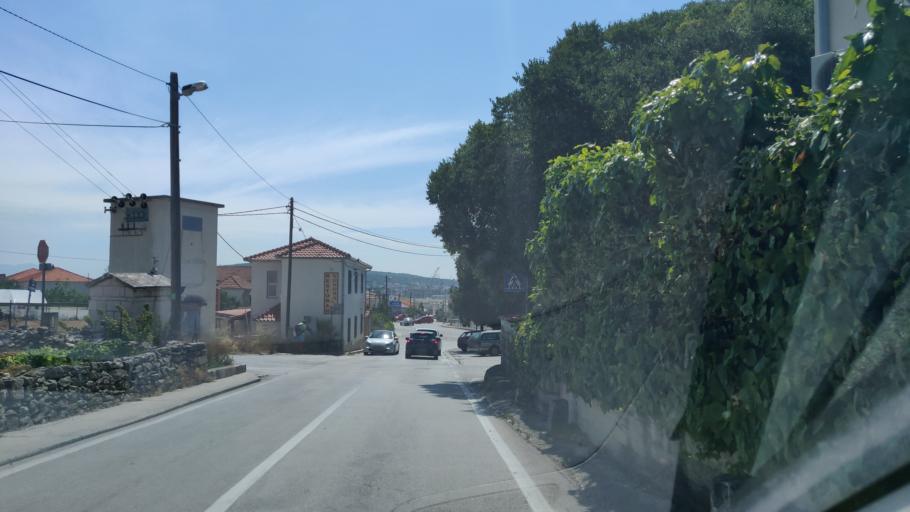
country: HR
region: Splitsko-Dalmatinska
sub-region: Grad Trogir
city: Trogir
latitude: 43.5195
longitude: 16.2282
